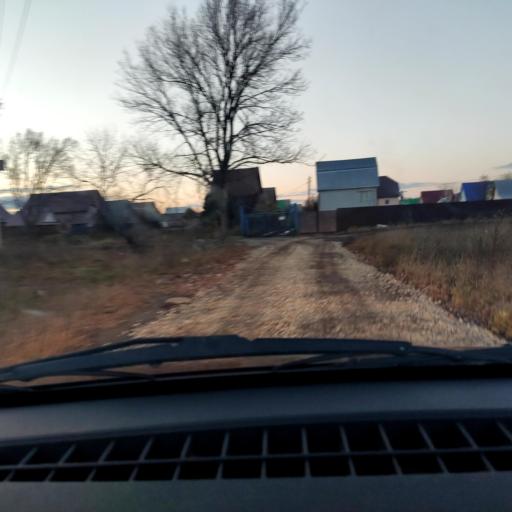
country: RU
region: Bashkortostan
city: Ufa
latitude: 54.6474
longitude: 55.8996
